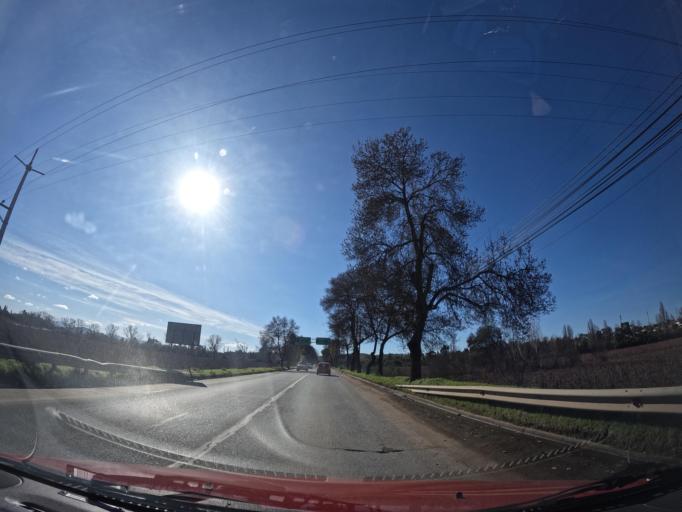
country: CL
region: Maule
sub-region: Provincia de Cauquenes
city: Cauquenes
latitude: -35.9611
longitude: -72.3121
